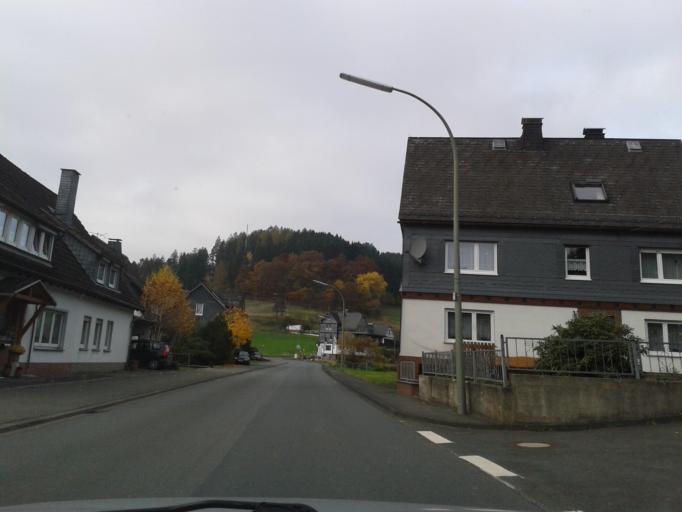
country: DE
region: North Rhine-Westphalia
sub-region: Regierungsbezirk Arnsberg
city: Bad Laasphe
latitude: 50.9233
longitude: 8.3789
